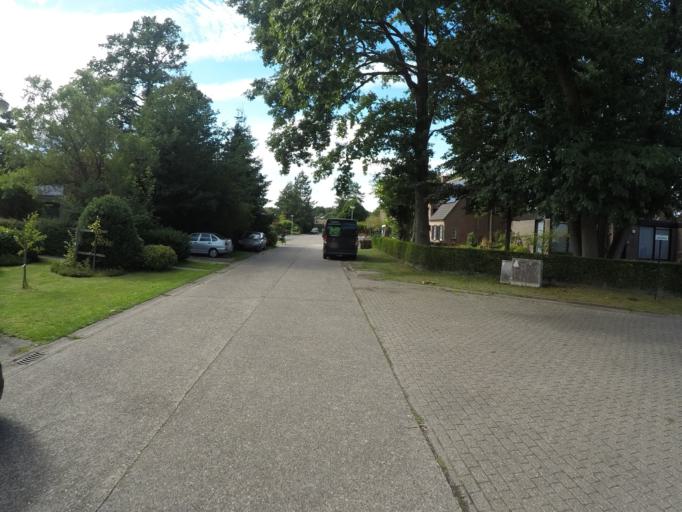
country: BE
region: Flanders
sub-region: Provincie Antwerpen
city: Lier
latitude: 51.1467
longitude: 4.6086
